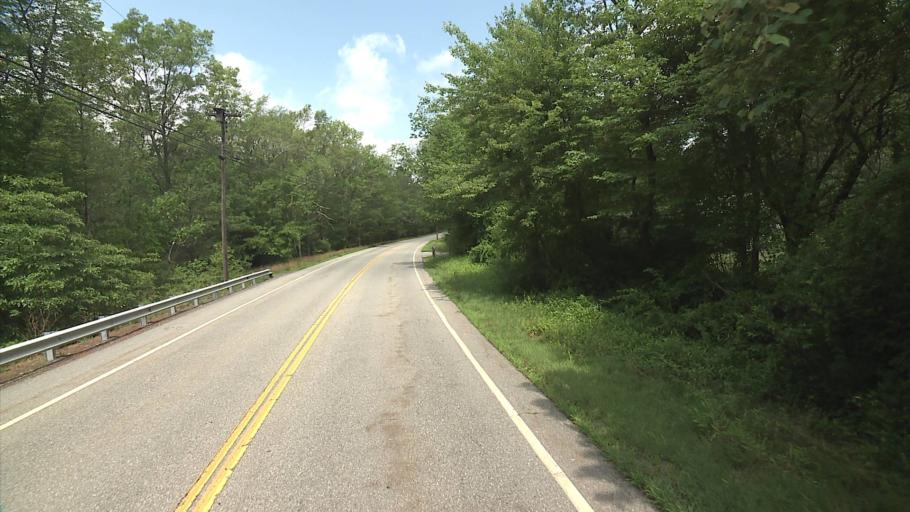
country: US
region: Rhode Island
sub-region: Washington County
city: Hopkinton
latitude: 41.5647
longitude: -71.8264
